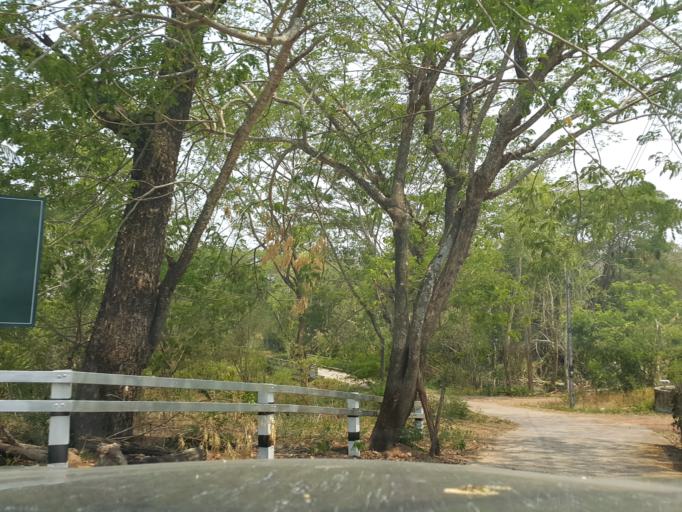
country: TH
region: Lampang
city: Mae Phrik
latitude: 17.5727
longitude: 99.0859
